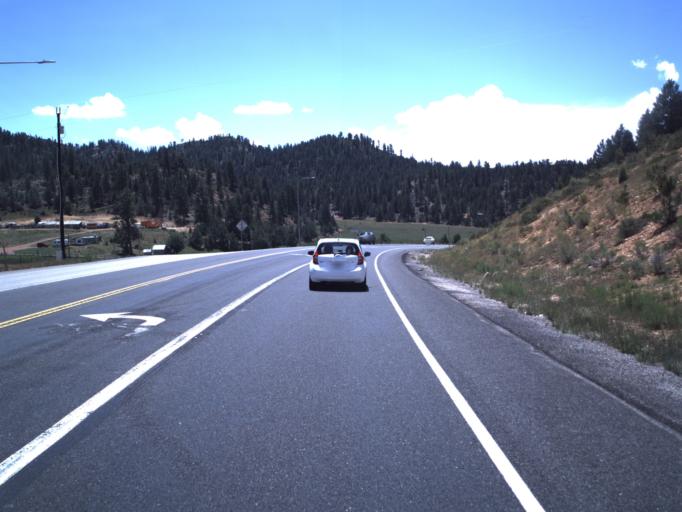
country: US
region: Utah
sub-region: Kane County
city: Kanab
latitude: 37.4282
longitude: -112.5383
